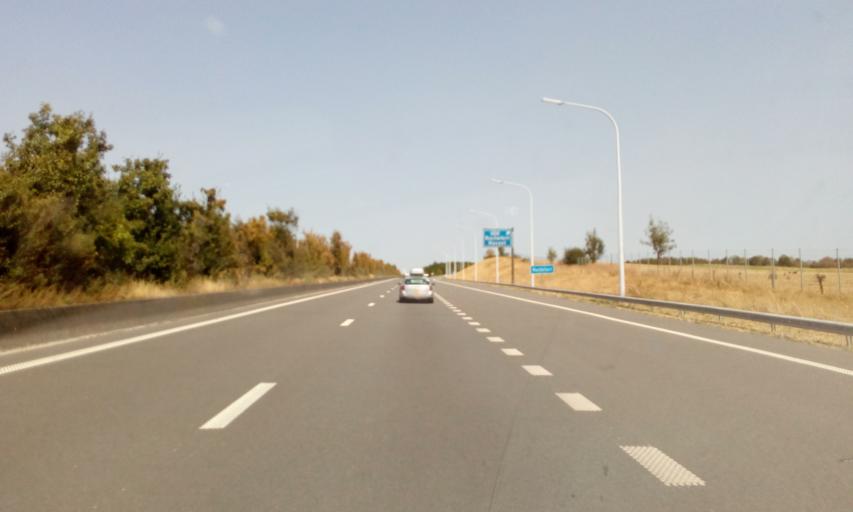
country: BE
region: Wallonia
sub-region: Province de Namur
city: Houyet
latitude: 50.1642
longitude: 5.0710
